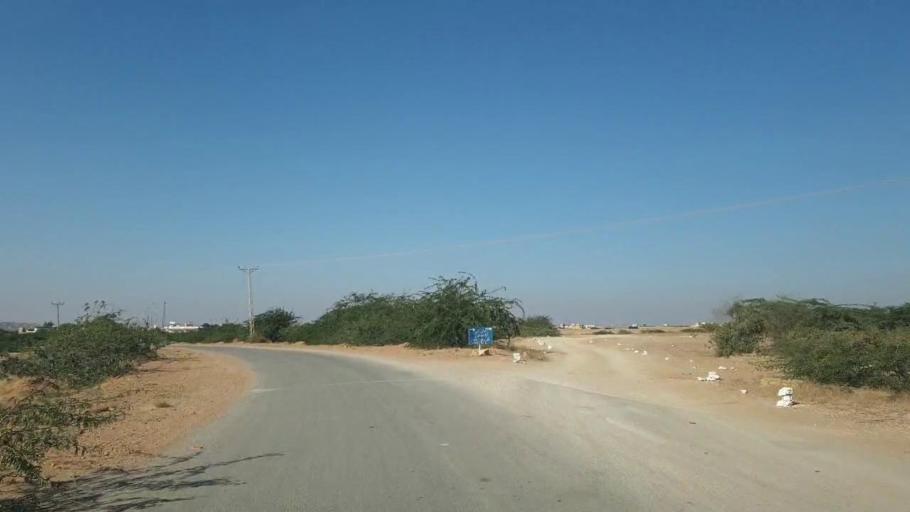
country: PK
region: Sindh
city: Malir Cantonment
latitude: 25.2870
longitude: 67.5779
